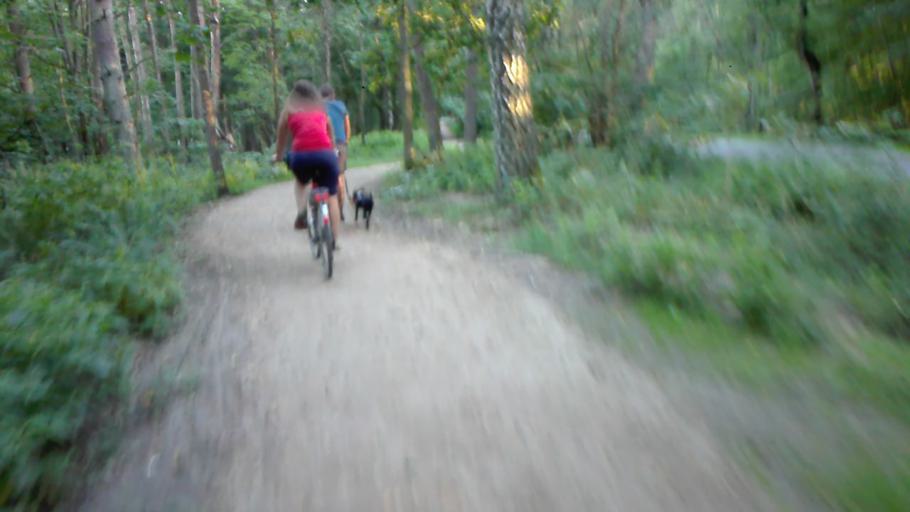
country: PL
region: West Pomeranian Voivodeship
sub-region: Powiat policki
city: Dobra
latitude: 53.4702
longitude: 14.3627
